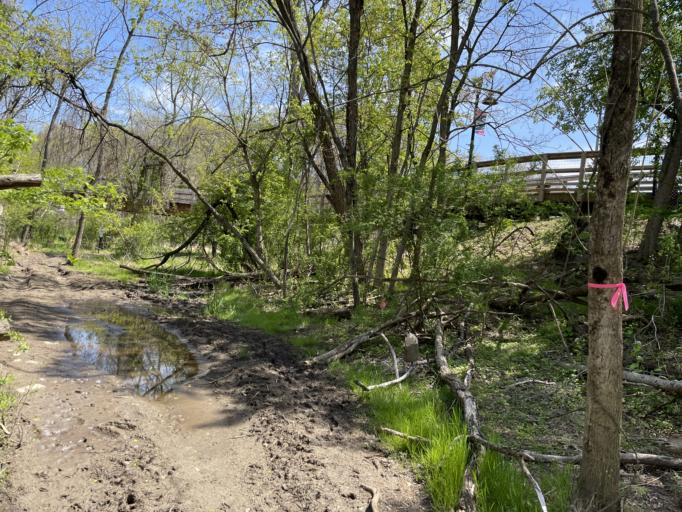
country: US
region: Maryland
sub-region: Baltimore County
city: Owings Mills
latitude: 39.4287
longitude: -76.7772
